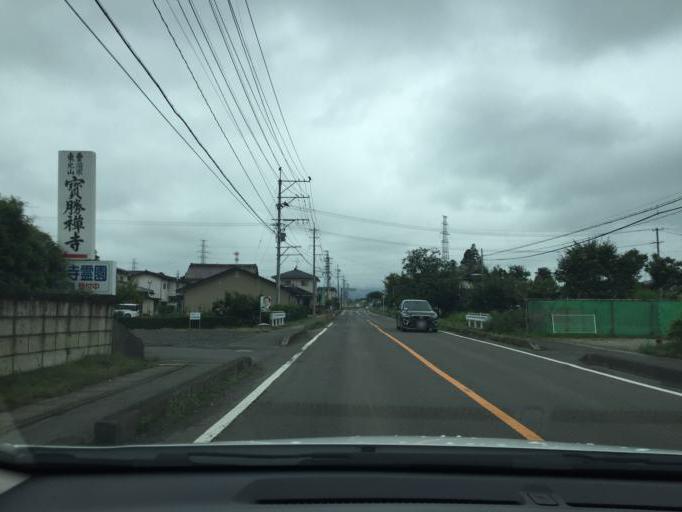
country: JP
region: Fukushima
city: Fukushima-shi
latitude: 37.7487
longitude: 140.4269
